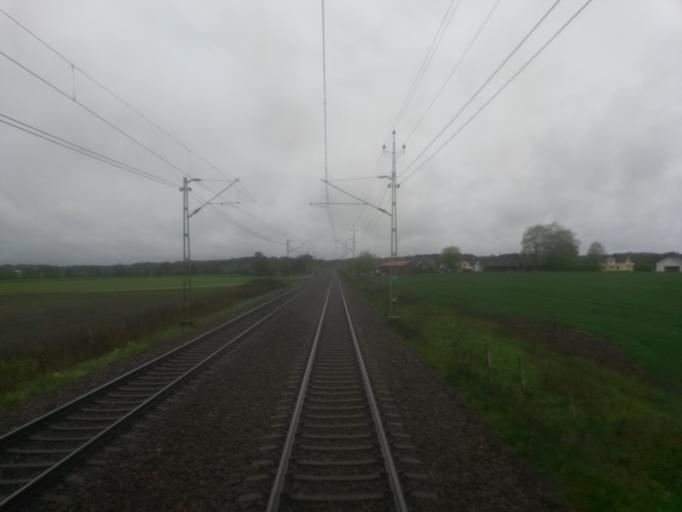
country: SE
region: Vaestra Goetaland
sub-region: Vargarda Kommun
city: Vargarda
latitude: 58.0286
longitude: 12.7700
